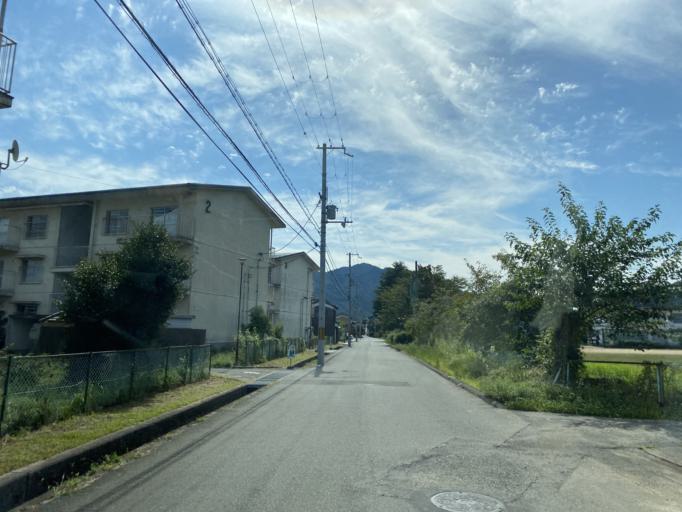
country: JP
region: Hyogo
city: Toyooka
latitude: 35.4327
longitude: 134.7928
